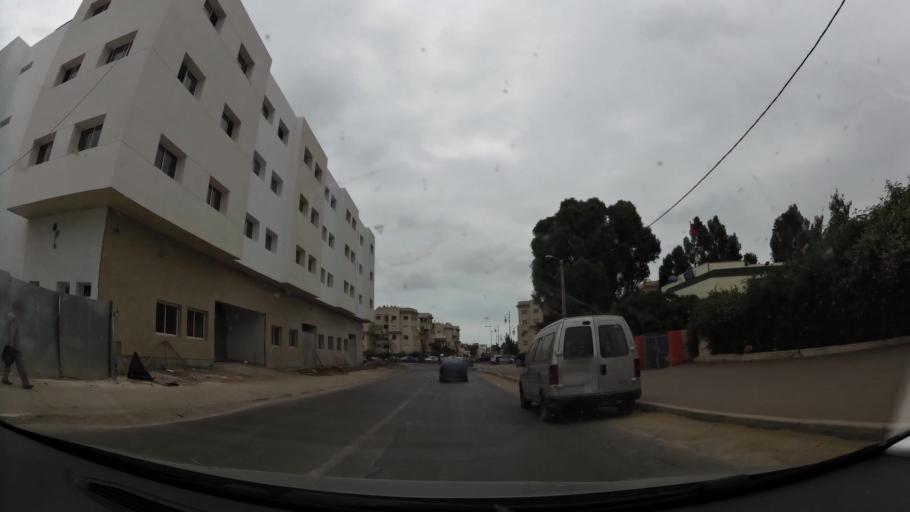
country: MA
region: Rabat-Sale-Zemmour-Zaer
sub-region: Rabat
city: Rabat
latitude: 33.9758
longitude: -6.8188
